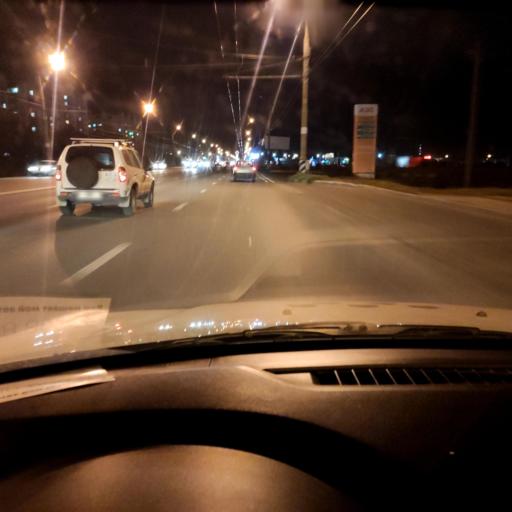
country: RU
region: Samara
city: Tol'yatti
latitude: 53.5500
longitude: 49.3280
